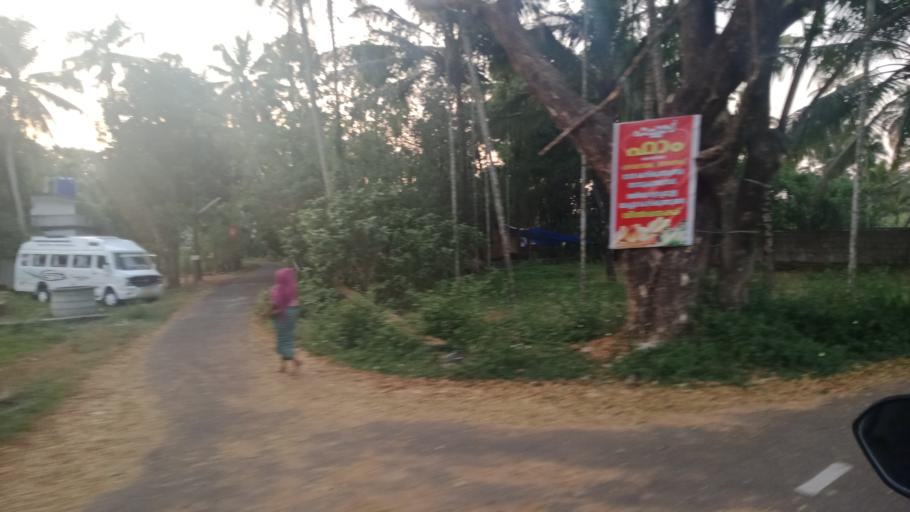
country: IN
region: Kerala
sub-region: Ernakulam
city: Angamali
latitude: 10.1939
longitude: 76.3088
